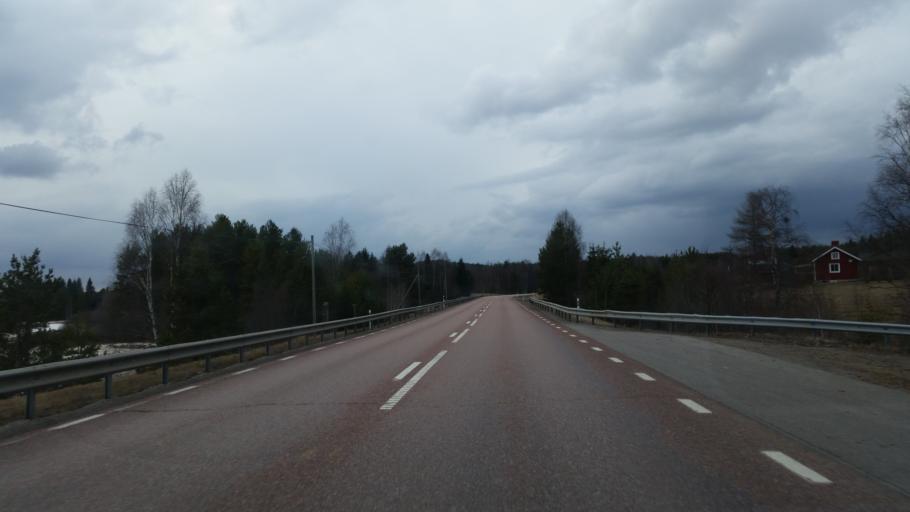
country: SE
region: Gaevleborg
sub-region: Ljusdals Kommun
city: Ljusdal
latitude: 61.7840
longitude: 16.1359
